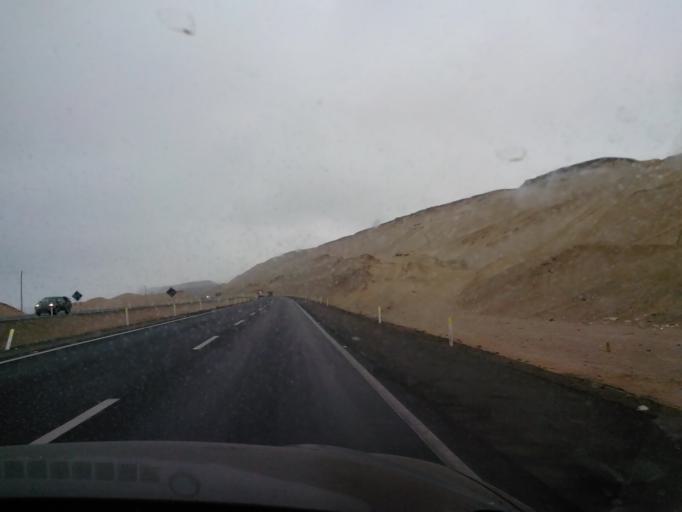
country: PE
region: Ica
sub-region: Provincia de Chincha
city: San Pedro
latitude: -13.3119
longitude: -76.2488
